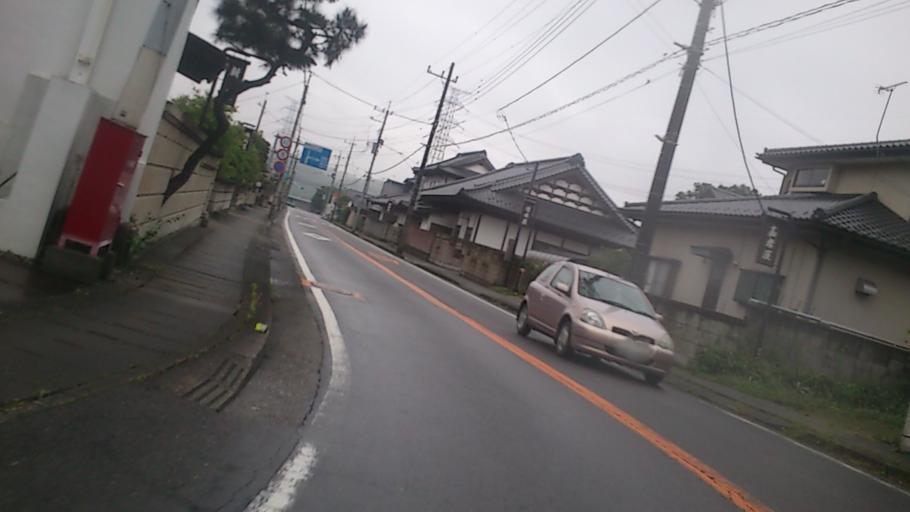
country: JP
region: Tochigi
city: Otawara
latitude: 36.7878
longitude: 140.1213
